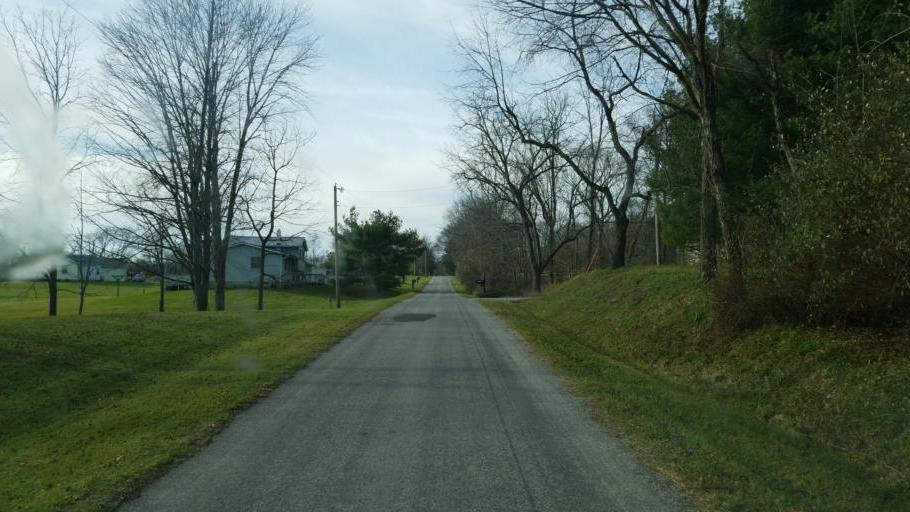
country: US
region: Ohio
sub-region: Knox County
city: Fredericktown
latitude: 40.4875
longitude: -82.6397
